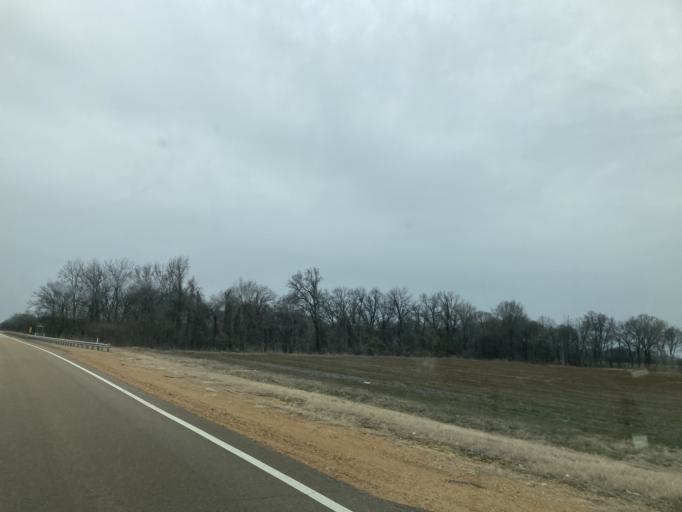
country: US
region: Mississippi
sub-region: Humphreys County
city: Belzoni
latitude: 33.0751
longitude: -90.4768
